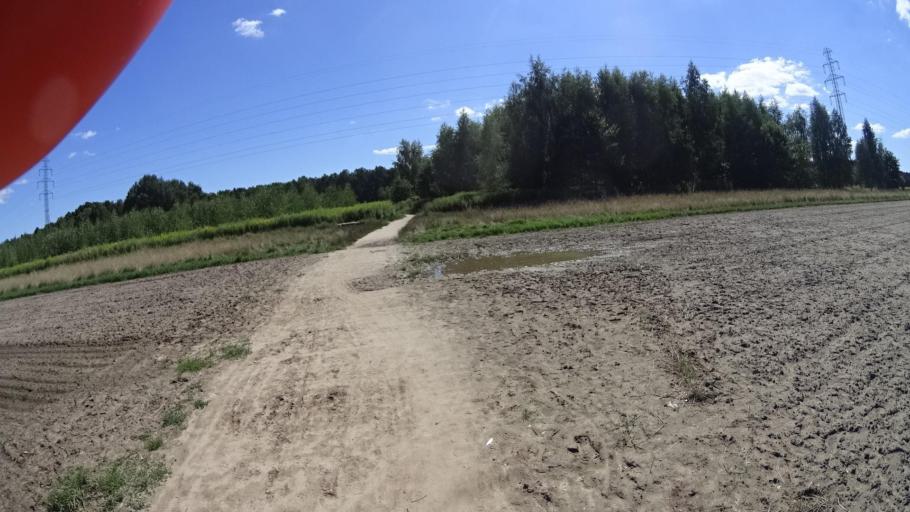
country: PL
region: Masovian Voivodeship
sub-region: Warszawa
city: Kabaty
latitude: 52.1271
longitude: 21.0751
